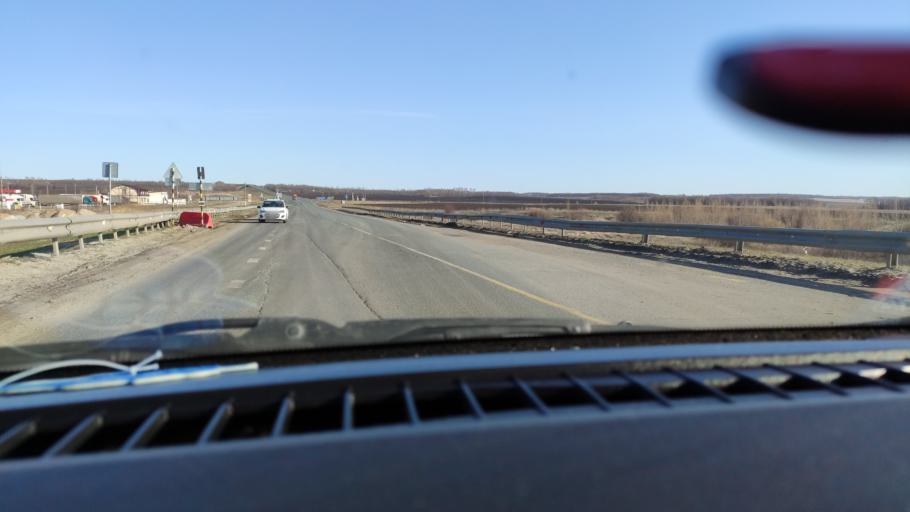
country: RU
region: Saratov
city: Dukhovnitskoye
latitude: 52.7395
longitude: 48.2542
